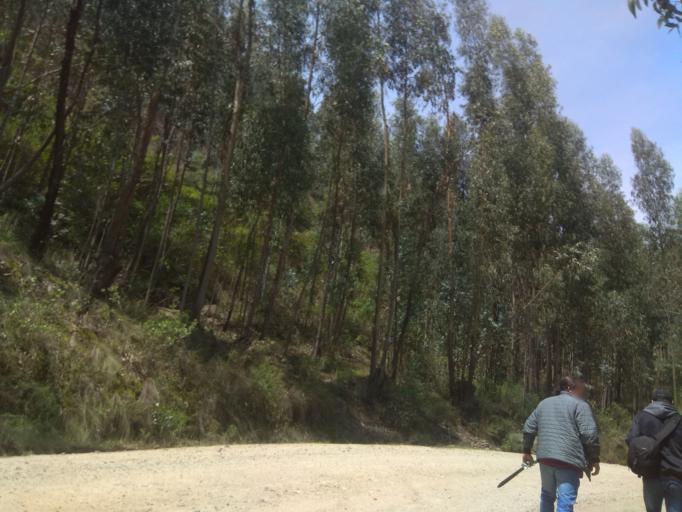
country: CO
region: Boyaca
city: Socha Viejo
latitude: 5.9786
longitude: -72.7249
